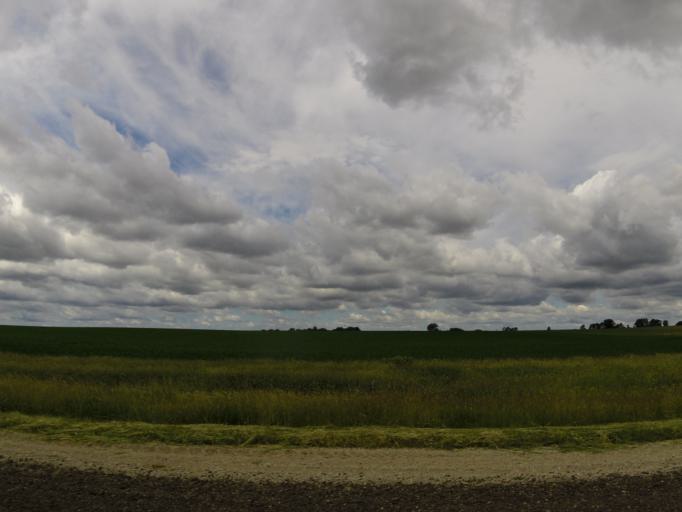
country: US
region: Iowa
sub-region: Howard County
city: Cresco
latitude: 43.4353
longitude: -92.2986
